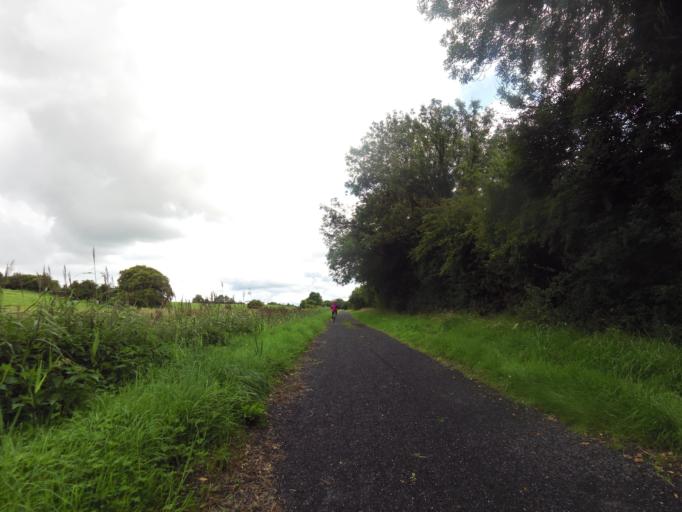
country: IE
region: Leinster
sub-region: An Iarmhi
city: An Muileann gCearr
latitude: 53.5177
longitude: -7.4344
